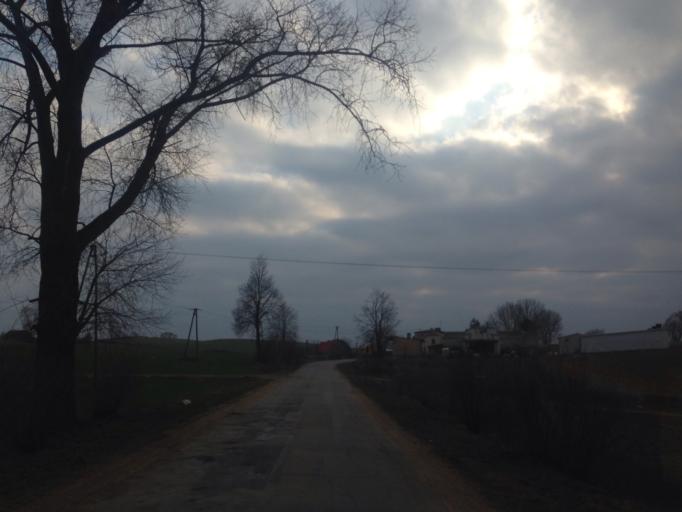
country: PL
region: Warmian-Masurian Voivodeship
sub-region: Powiat dzialdowski
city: Lidzbark
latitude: 53.3544
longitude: 19.7610
